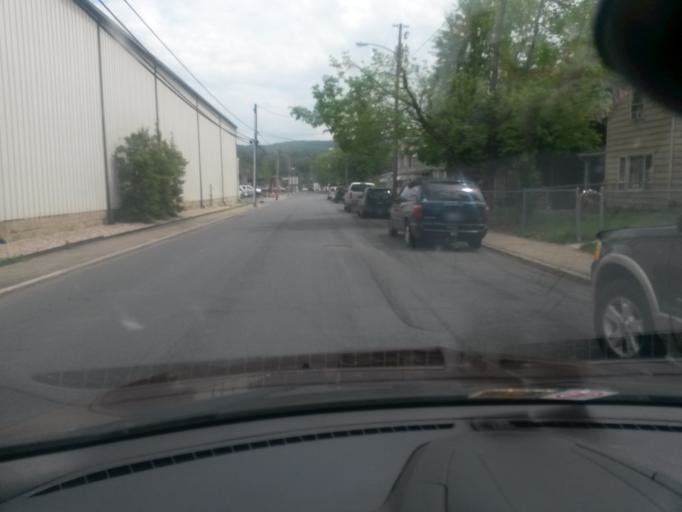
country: US
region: Virginia
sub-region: City of Covington
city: Covington
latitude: 37.7857
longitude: -79.9929
